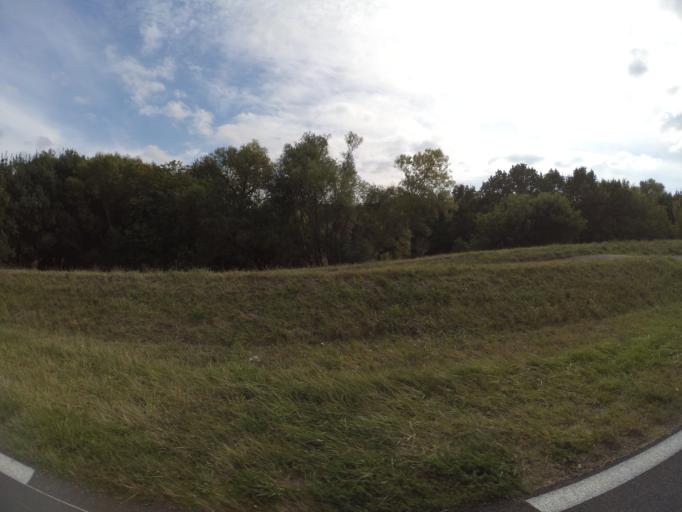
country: FR
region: Centre
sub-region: Departement d'Indre-et-Loire
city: Langeais
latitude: 47.2982
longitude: 0.3443
